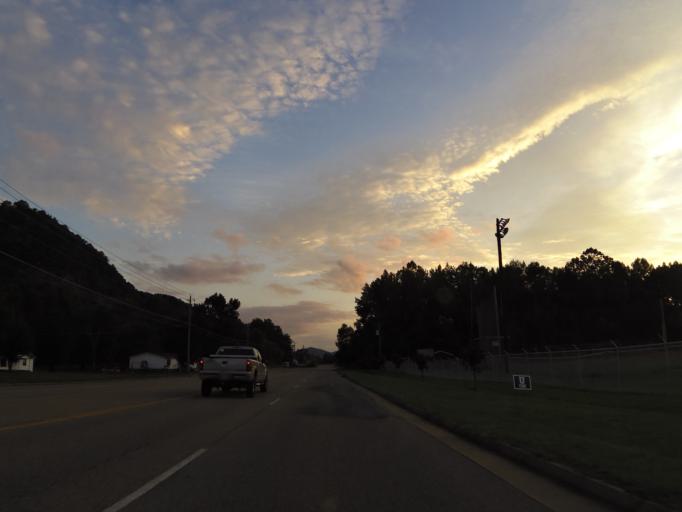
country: US
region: Tennessee
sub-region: Carter County
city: Hunter
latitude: 36.3831
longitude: -82.1443
